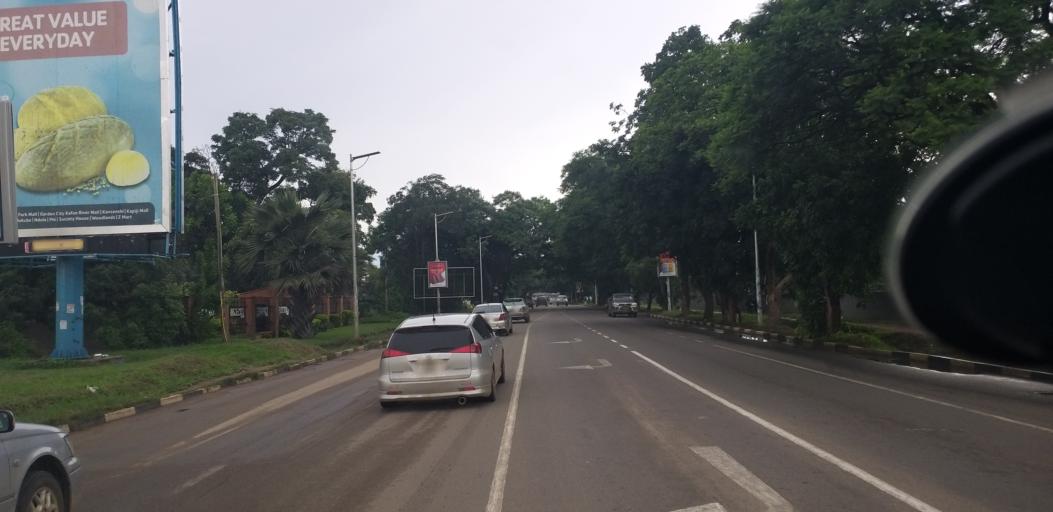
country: ZM
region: Lusaka
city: Lusaka
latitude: -15.4149
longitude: 28.2891
